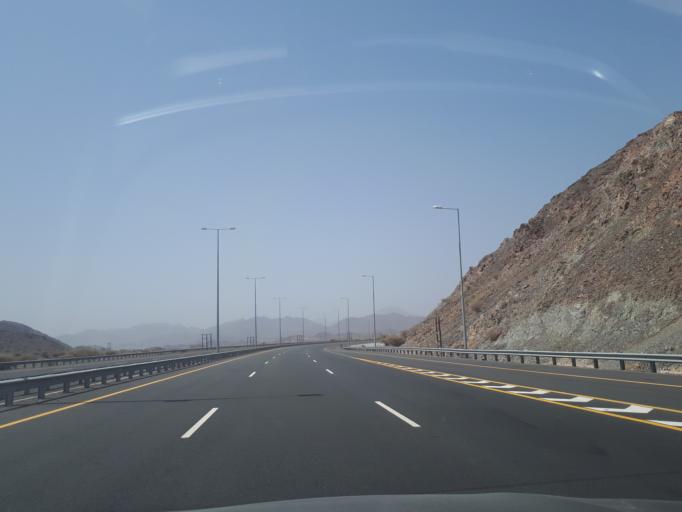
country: OM
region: Muhafazat ad Dakhiliyah
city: Bidbid
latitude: 23.3190
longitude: 58.1149
